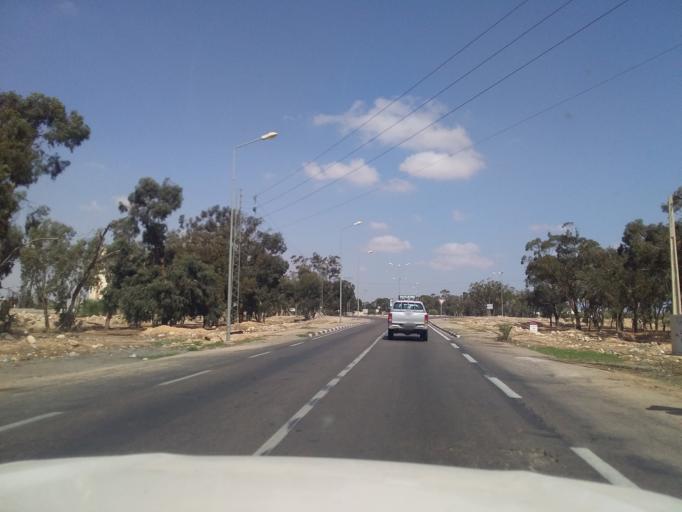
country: TN
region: Madanin
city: Medenine
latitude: 33.5979
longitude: 10.3100
